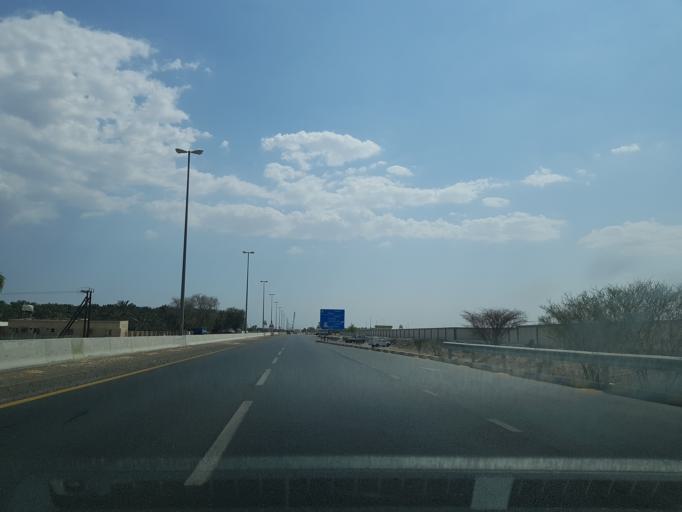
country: AE
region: Ash Shariqah
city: Adh Dhayd
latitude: 25.2365
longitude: 55.9164
